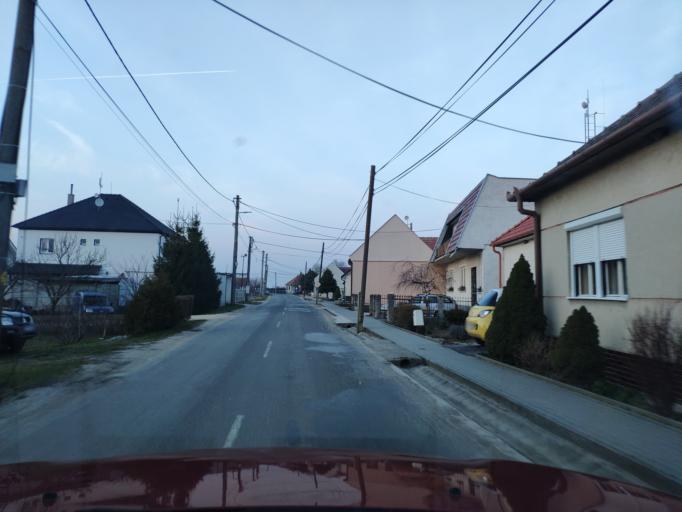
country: SK
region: Trnavsky
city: Leopoldov
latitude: 48.4655
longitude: 17.7210
